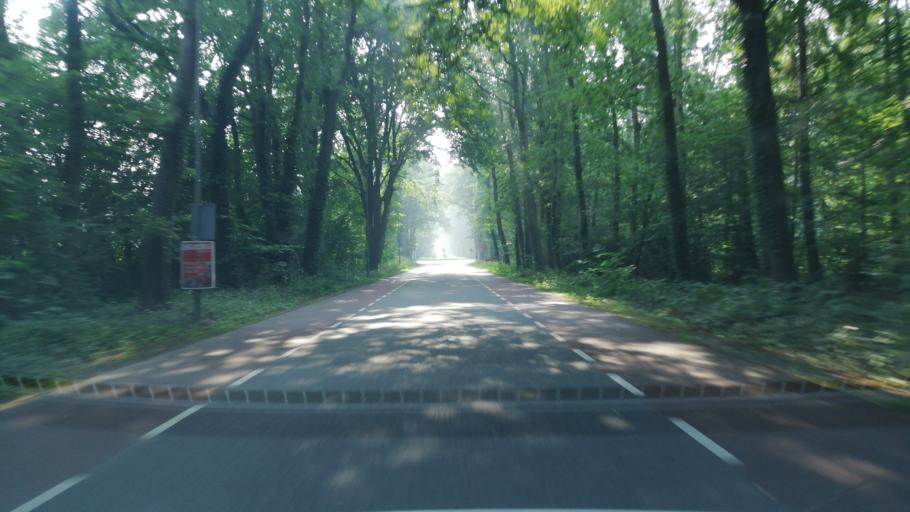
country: NL
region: Gelderland
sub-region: Gemeente Ermelo
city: Ermelo
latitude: 52.2918
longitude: 5.6416
